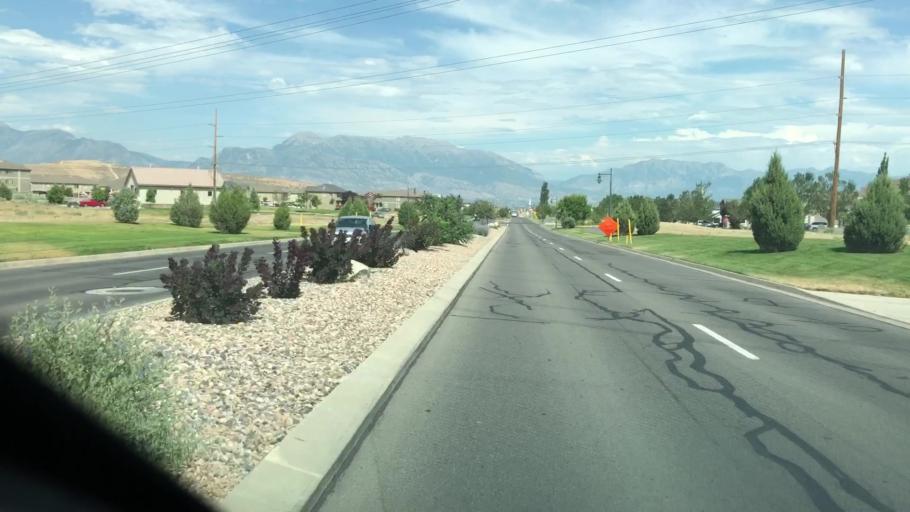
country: US
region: Utah
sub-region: Utah County
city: Eagle Mountain
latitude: 40.3621
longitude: -111.9738
